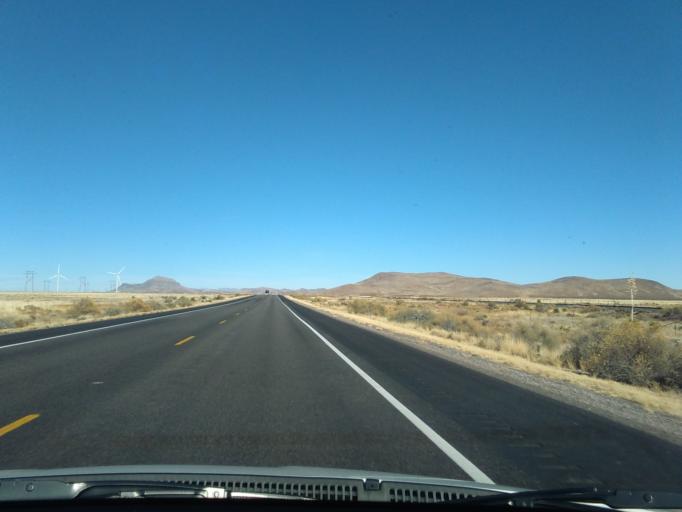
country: US
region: New Mexico
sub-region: Luna County
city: Deming
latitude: 32.5104
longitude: -107.5050
